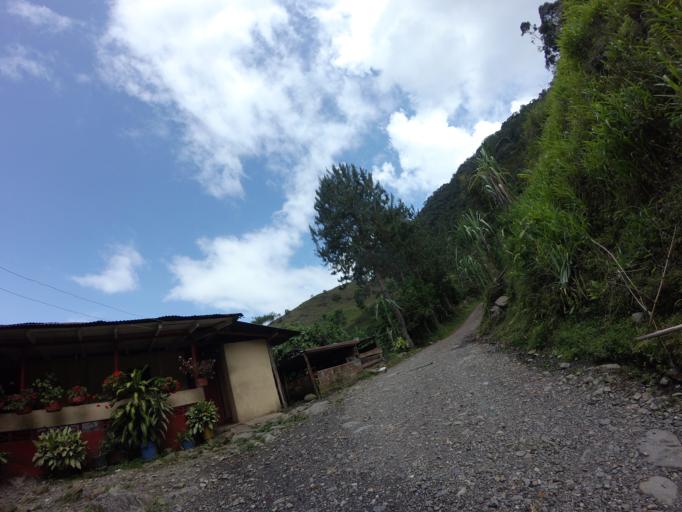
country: CO
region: Caldas
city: Pensilvania
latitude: 5.4578
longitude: -75.1730
